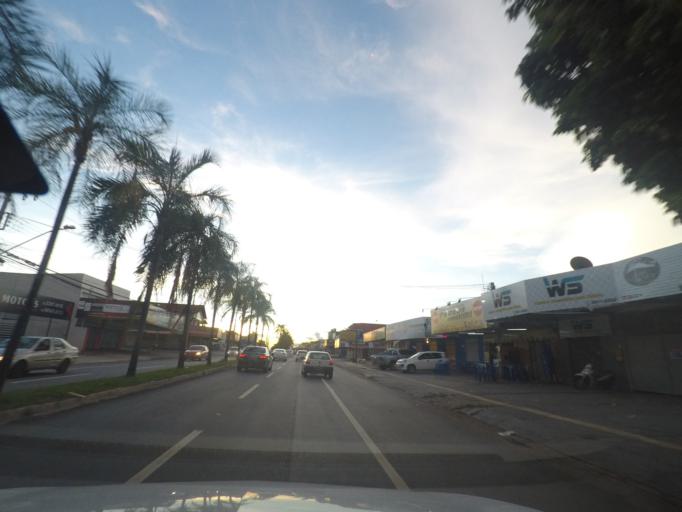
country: BR
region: Goias
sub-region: Goiania
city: Goiania
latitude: -16.6963
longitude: -49.3021
